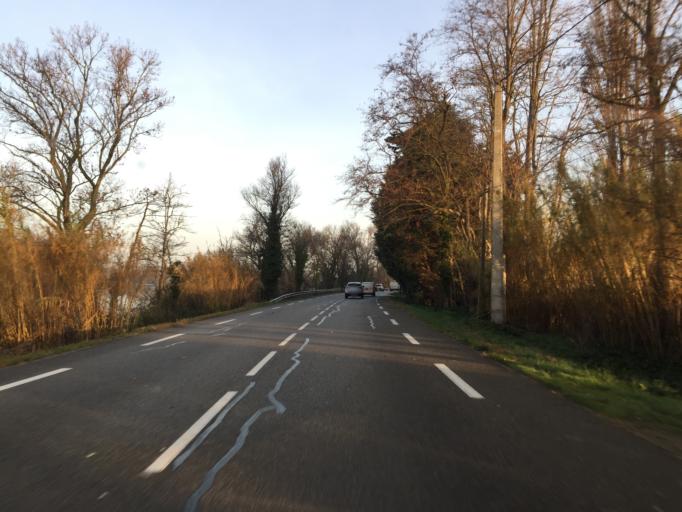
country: FR
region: Languedoc-Roussillon
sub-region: Departement du Gard
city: Montfaucon
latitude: 44.0820
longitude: 4.7611
